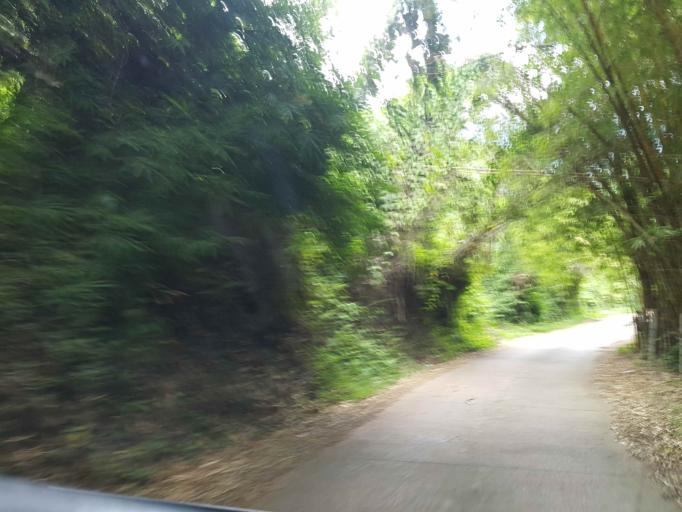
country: TH
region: Chiang Mai
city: Hang Dong
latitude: 18.7758
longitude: 98.8486
